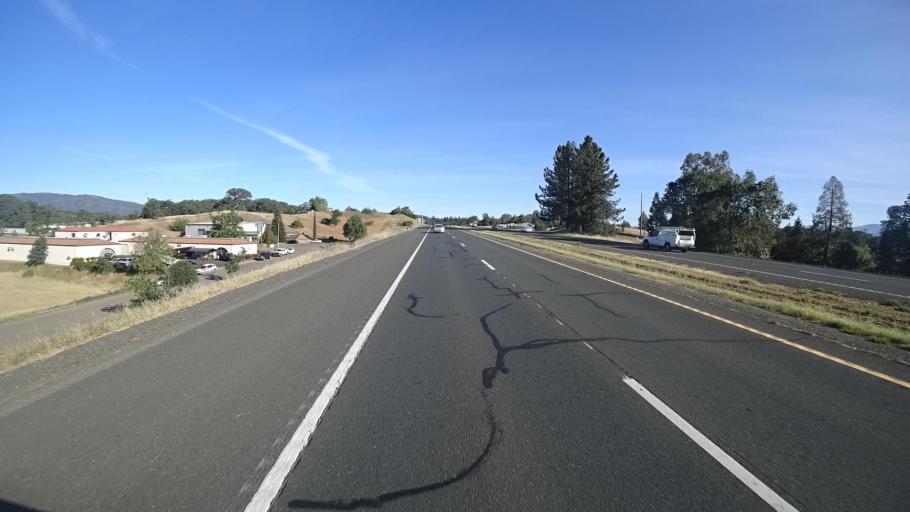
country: US
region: California
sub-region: Lake County
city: Lakeport
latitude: 39.0374
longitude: -122.9275
